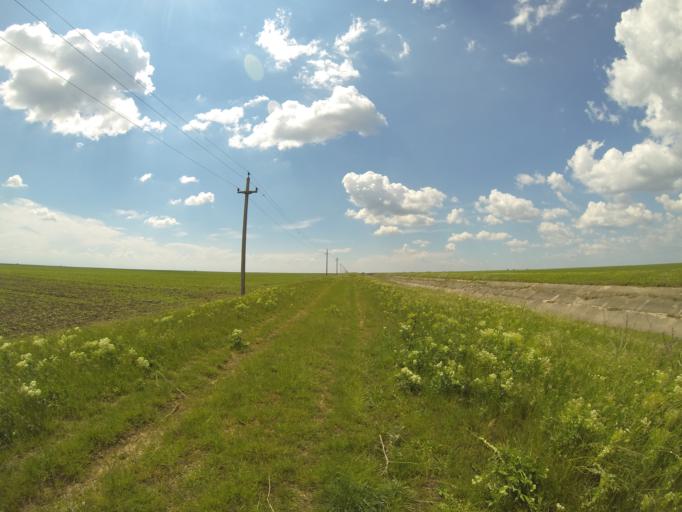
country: RO
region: Dolj
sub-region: Comuna Dranicu
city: Padea
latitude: 44.0132
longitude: 23.8207
